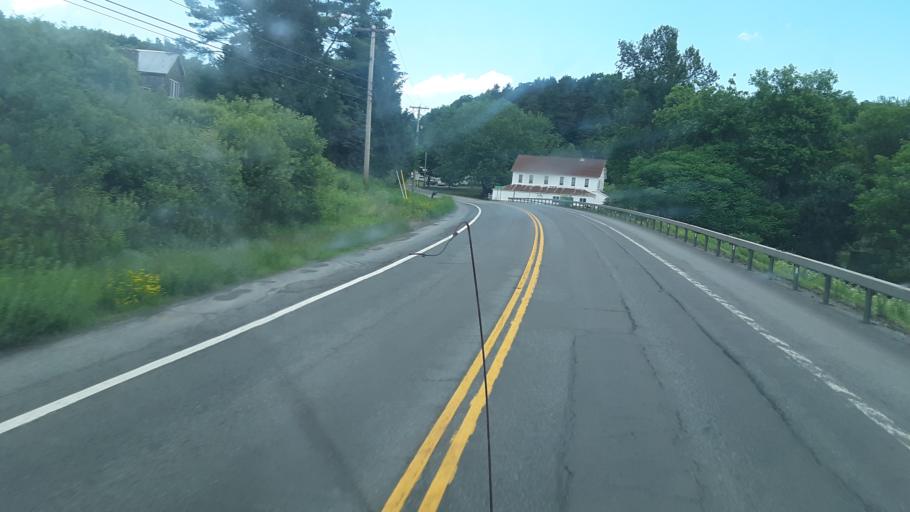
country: US
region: New York
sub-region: Oneida County
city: Rome
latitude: 43.3708
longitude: -75.4812
